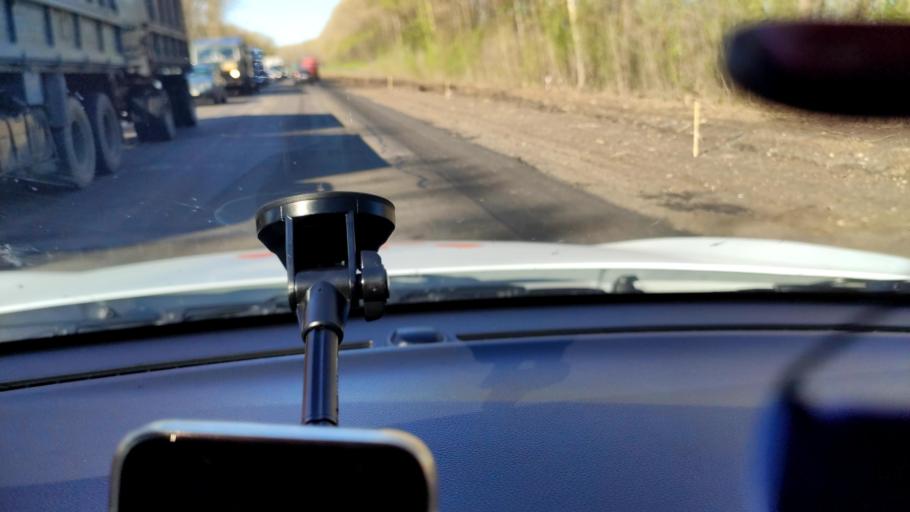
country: RU
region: Voronezj
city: Uryv-Pokrovka
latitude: 51.1839
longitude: 39.0838
